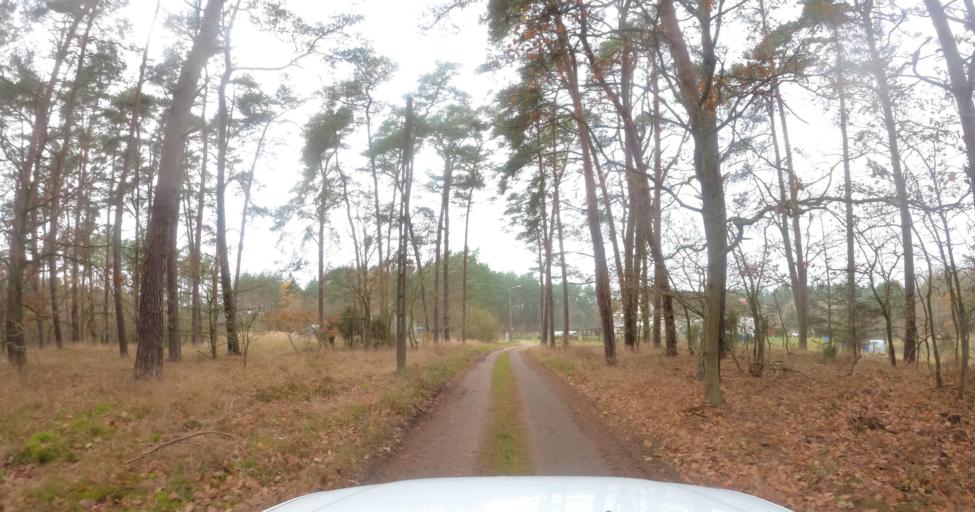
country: PL
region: West Pomeranian Voivodeship
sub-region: Powiat goleniowski
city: Przybiernow
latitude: 53.7665
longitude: 14.7399
